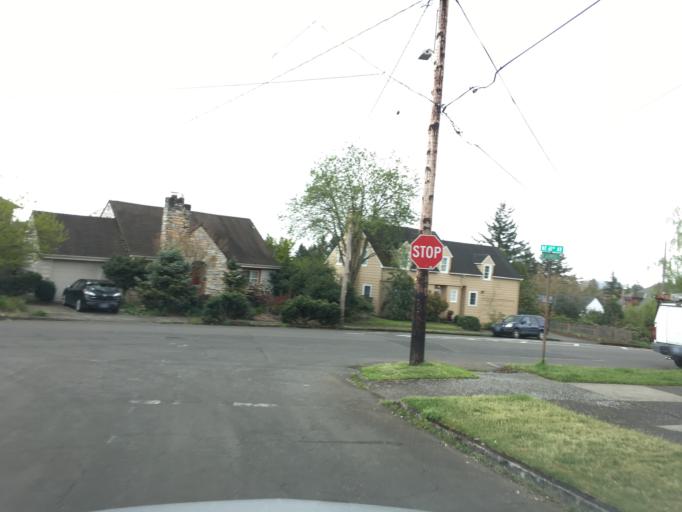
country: US
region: Oregon
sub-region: Multnomah County
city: Lents
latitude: 45.5401
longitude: -122.6006
